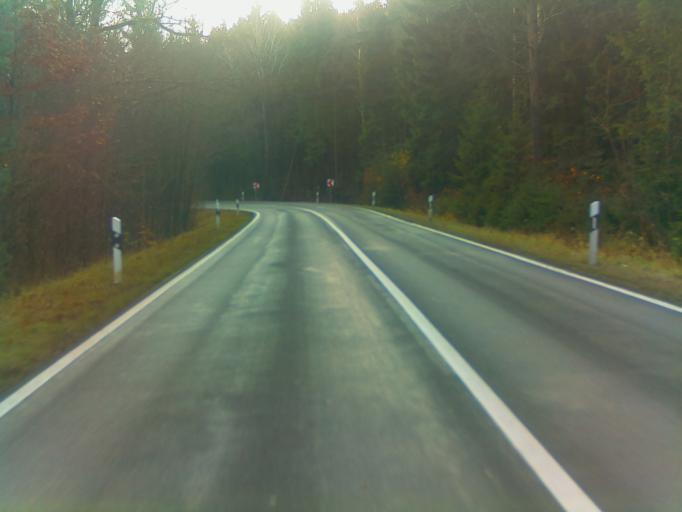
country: DE
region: Thuringia
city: Hildburghausen
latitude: 50.4561
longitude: 10.7441
